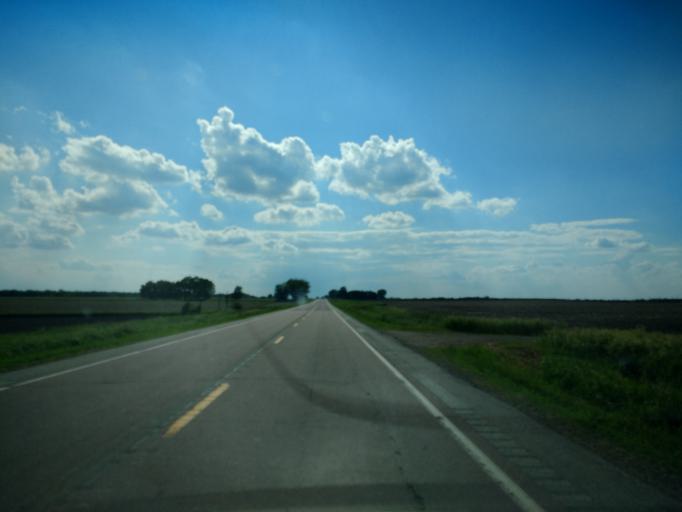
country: US
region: Iowa
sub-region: Clay County
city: Spencer
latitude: 43.1840
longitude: -95.1593
